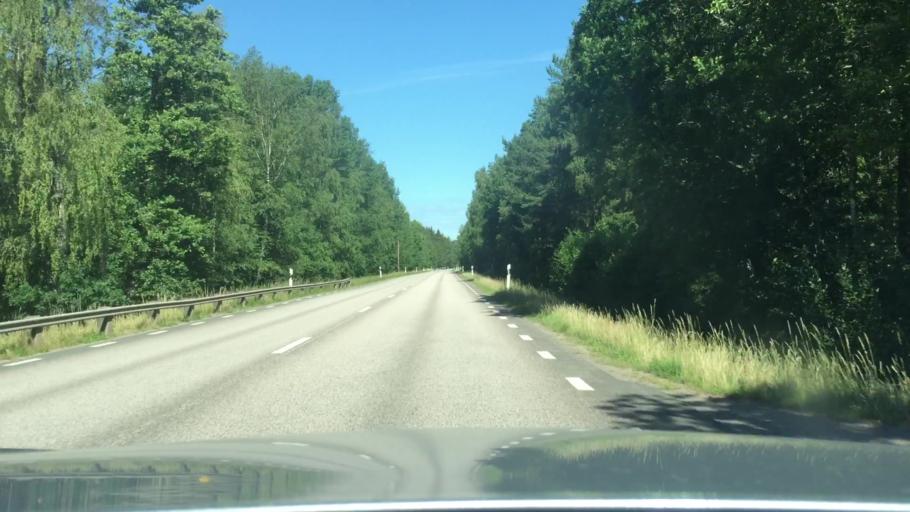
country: SE
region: Vaestra Goetaland
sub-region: Mariestads Kommun
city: Mariestad
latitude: 58.6740
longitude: 13.8528
